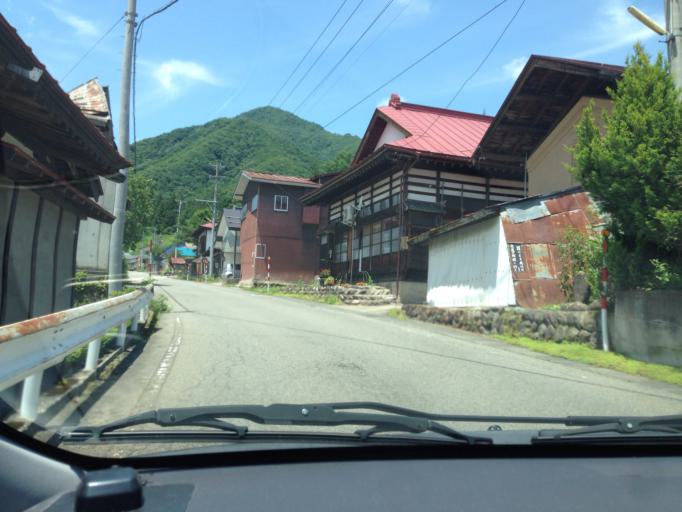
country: JP
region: Tochigi
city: Kuroiso
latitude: 37.2687
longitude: 139.8478
